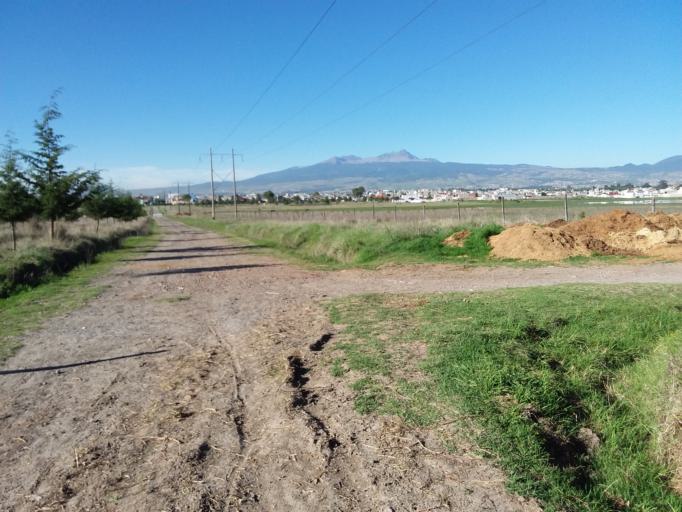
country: MX
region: Mexico
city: San Marcos Yachihuacaltepec
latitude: 19.3114
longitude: -99.6958
